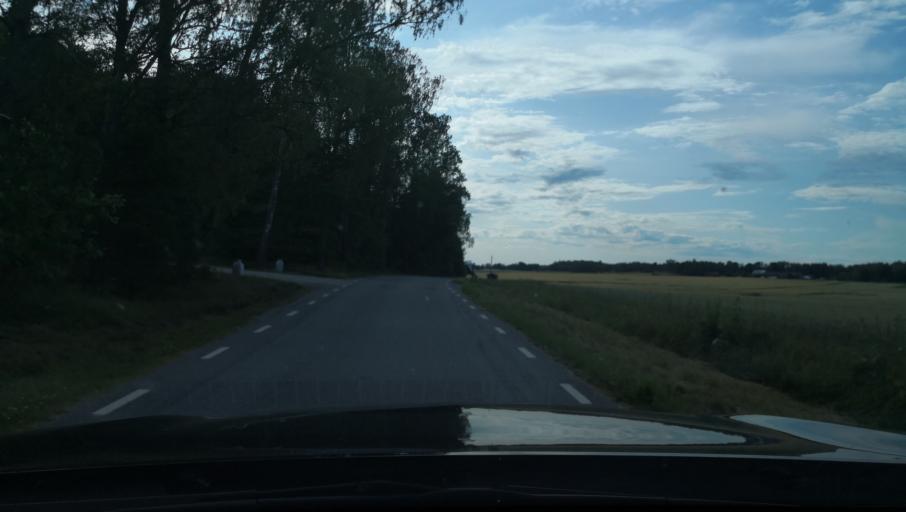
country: SE
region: Uppsala
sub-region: Enkopings Kommun
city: Orsundsbro
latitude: 59.6925
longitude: 17.3542
